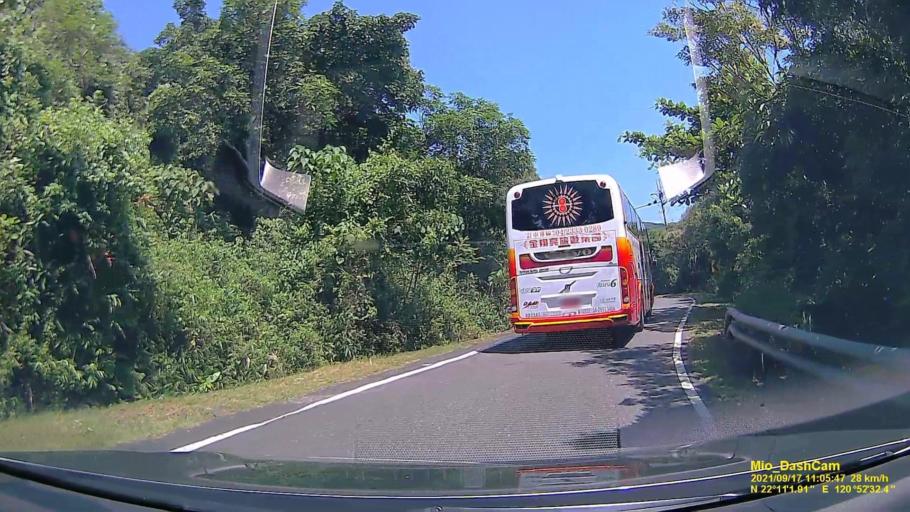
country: TW
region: Taiwan
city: Hengchun
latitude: 22.1839
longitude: 120.8757
